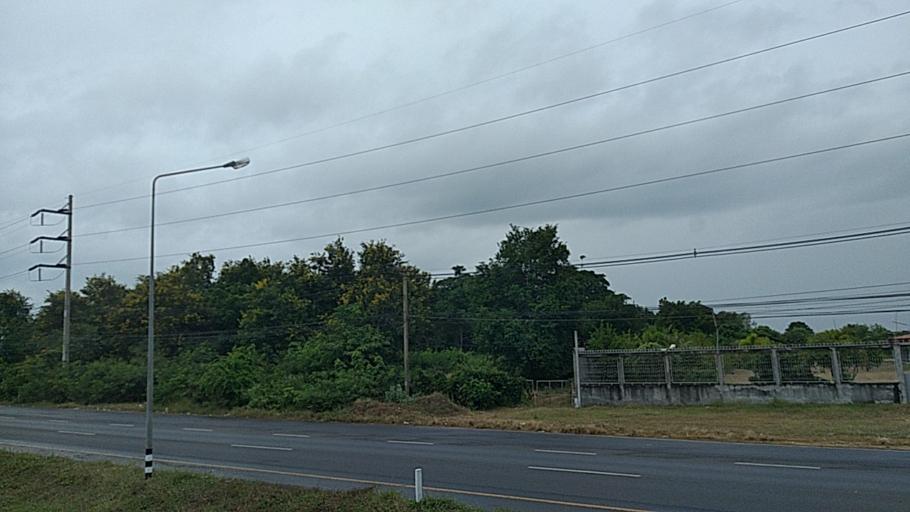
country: TH
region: Maha Sarakham
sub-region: Amphoe Borabue
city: Borabue
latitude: 16.0609
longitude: 103.1384
